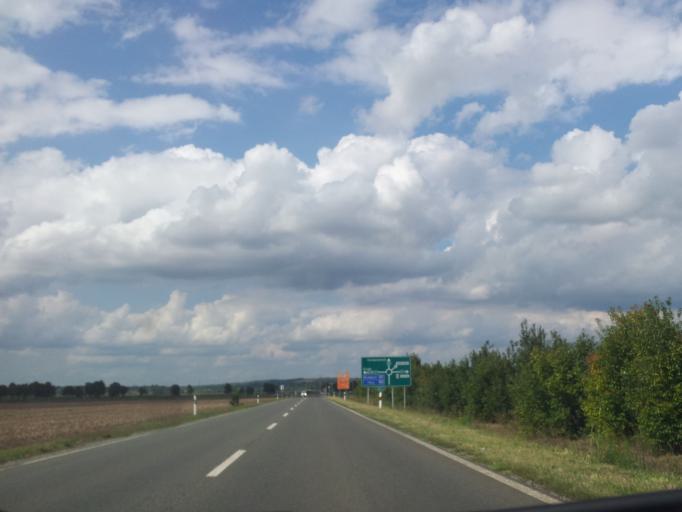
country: HU
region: Baranya
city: Mohacs
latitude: 45.9942
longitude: 18.6547
